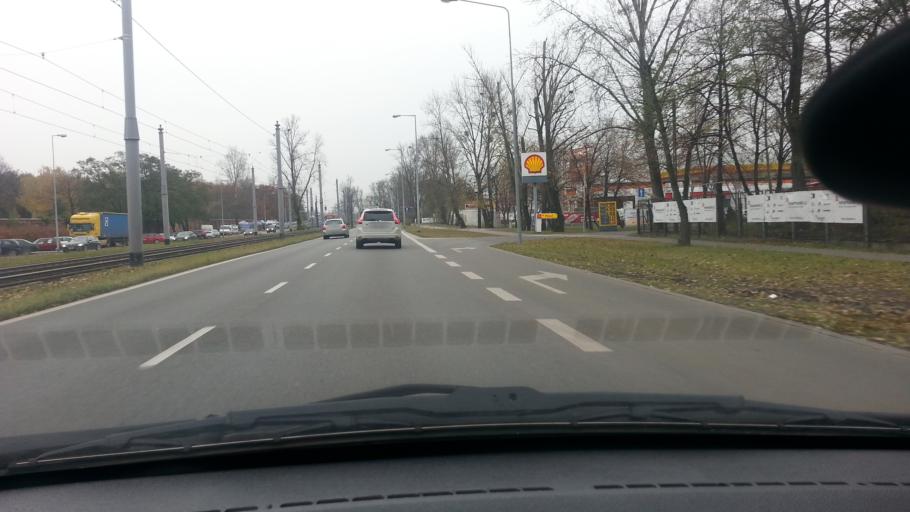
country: PL
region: Masovian Voivodeship
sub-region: Warszawa
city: Praga Polnoc
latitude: 52.2754
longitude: 21.0300
